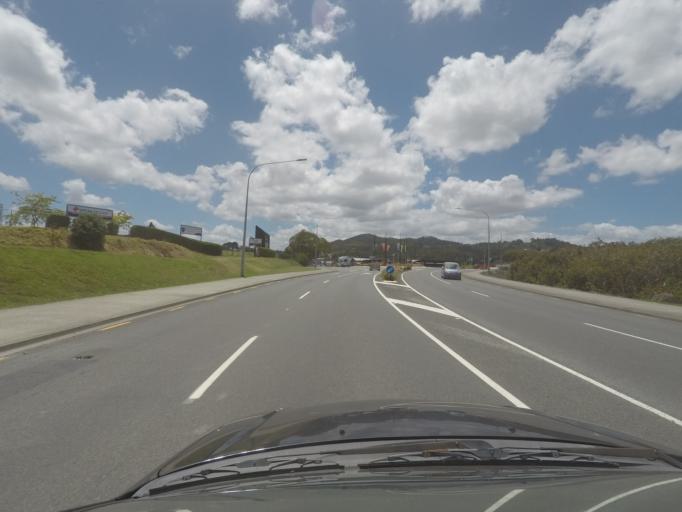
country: NZ
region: Northland
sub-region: Whangarei
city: Whangarei
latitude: -35.7359
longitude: 174.3326
